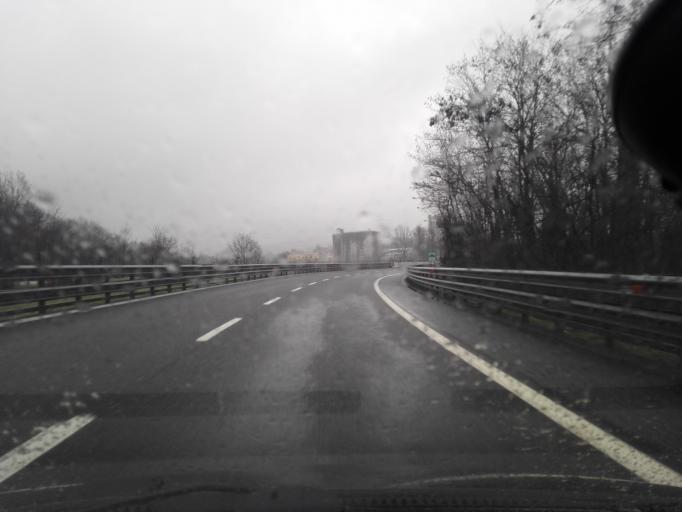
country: IT
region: Piedmont
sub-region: Provincia di Alessandria
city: Stazzano
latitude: 44.7107
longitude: 8.8727
